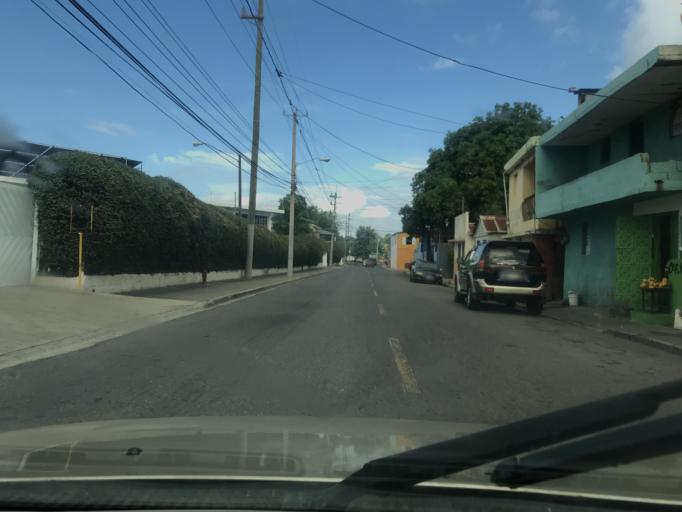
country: DO
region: Santiago
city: Santiago de los Caballeros
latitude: 19.4703
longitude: -70.7144
